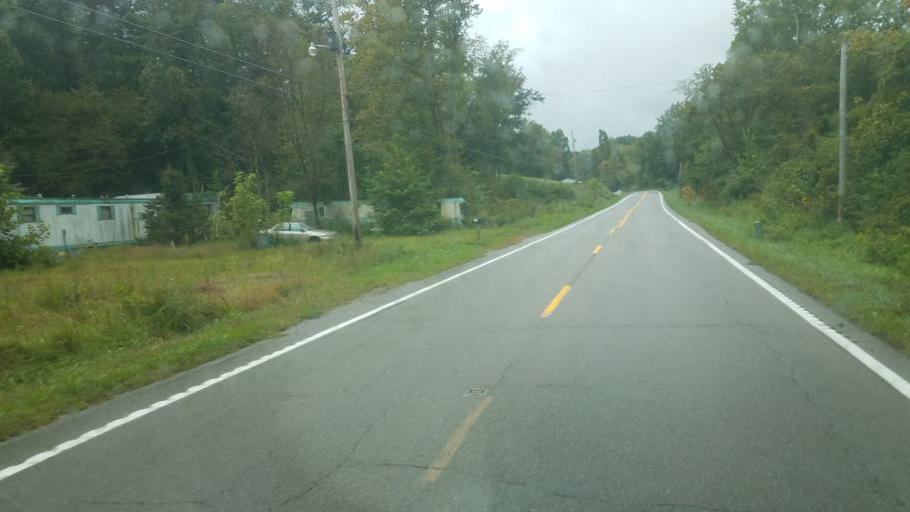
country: US
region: Ohio
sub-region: Jackson County
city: Oak Hill
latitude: 38.8571
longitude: -82.6288
